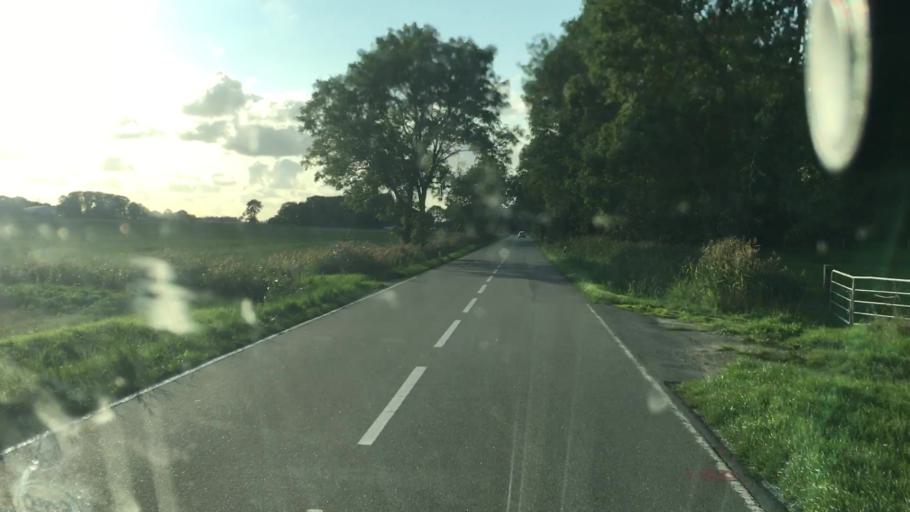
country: DE
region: Lower Saxony
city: Wittmund
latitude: 53.6416
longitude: 7.8166
